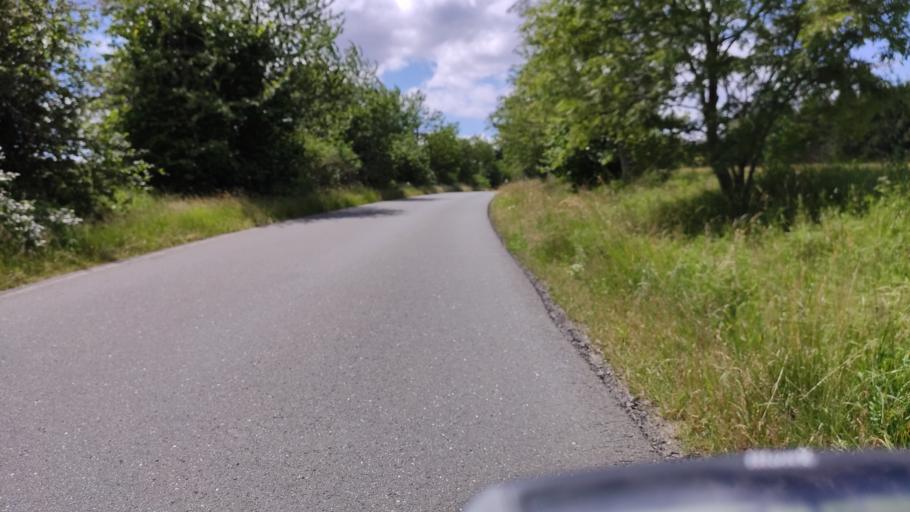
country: DE
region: Thuringia
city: Wurzbach
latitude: 50.4820
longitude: 11.5079
